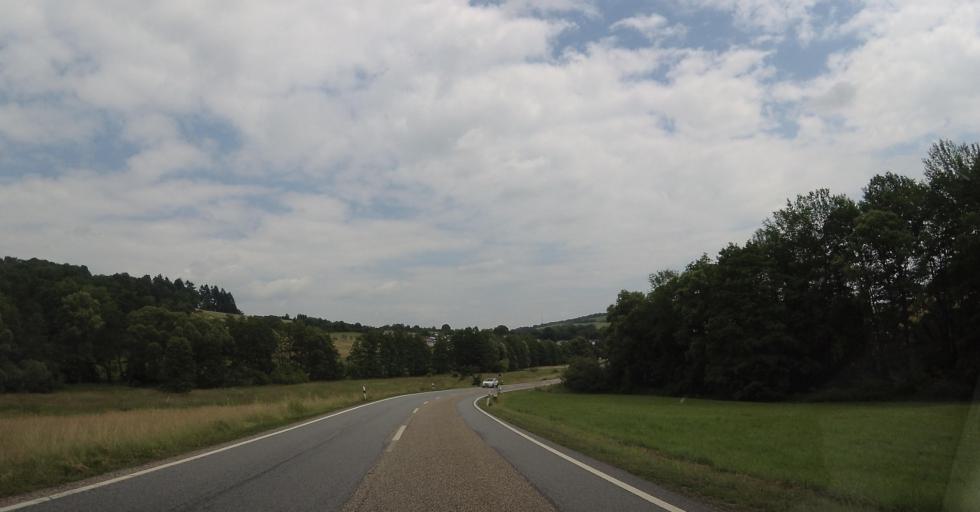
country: DE
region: Rheinland-Pfalz
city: Breitenbach
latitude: 49.4535
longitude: 7.2211
